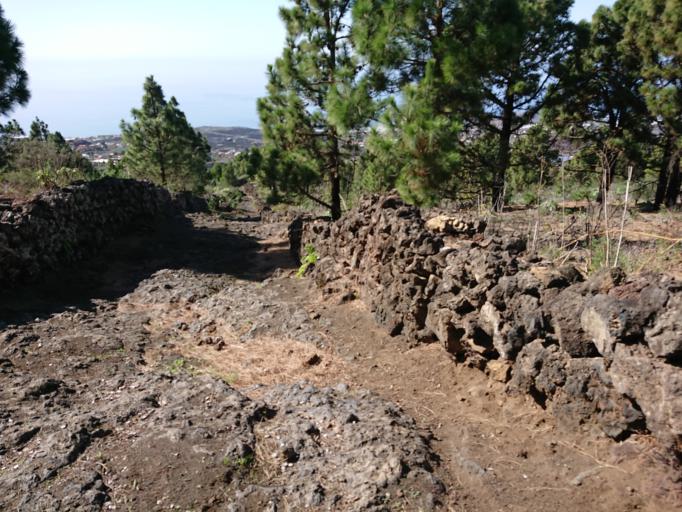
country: ES
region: Canary Islands
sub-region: Provincia de Santa Cruz de Tenerife
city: El Paso
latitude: 28.6056
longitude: -17.8705
